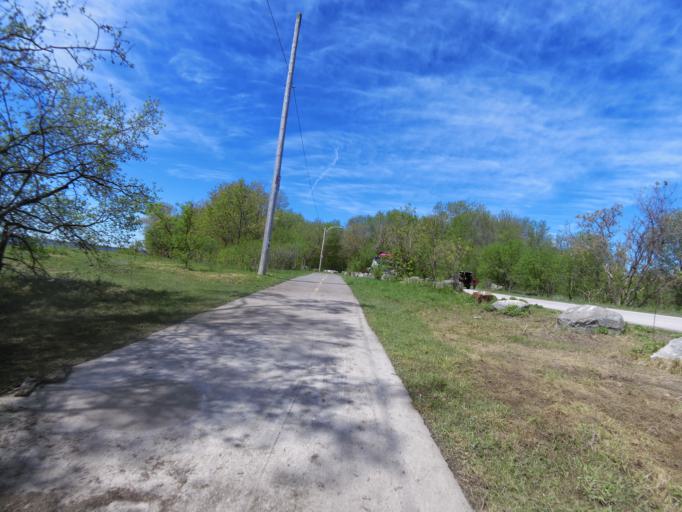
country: CA
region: Ontario
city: Bells Corners
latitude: 45.3800
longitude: -75.8057
